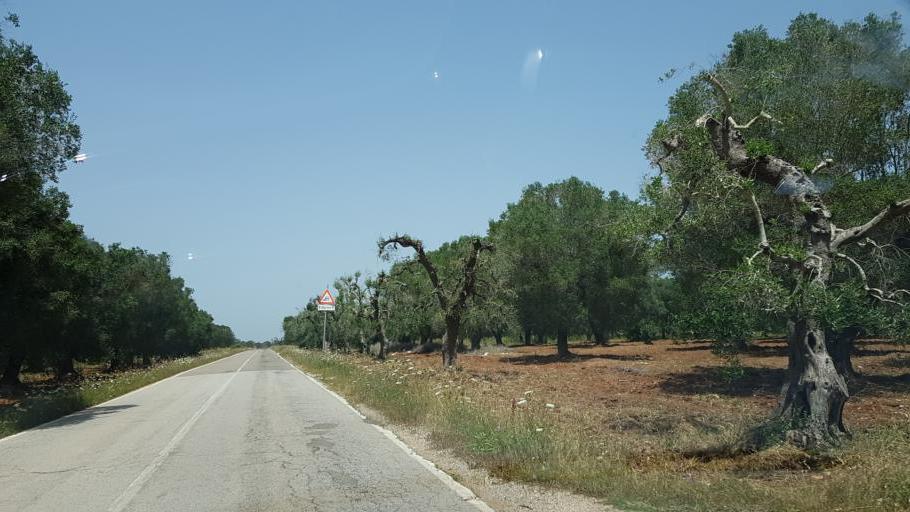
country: IT
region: Apulia
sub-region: Provincia di Brindisi
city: San Pancrazio Salentino
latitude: 40.4595
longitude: 17.8394
